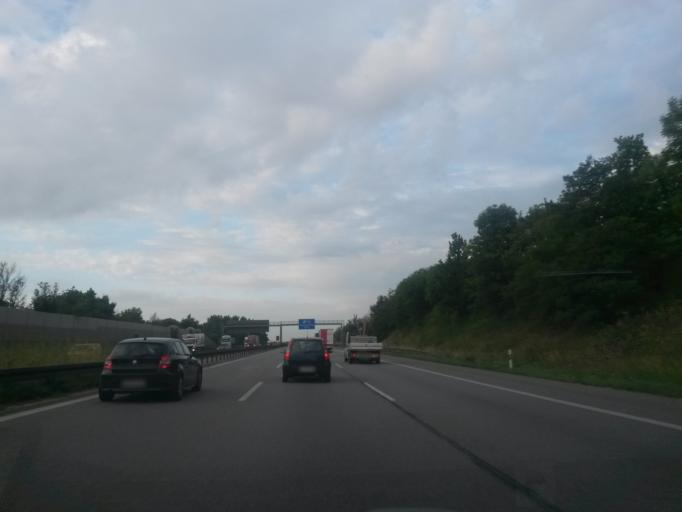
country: DE
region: Bavaria
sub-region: Upper Bavaria
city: Lenting
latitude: 48.7665
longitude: 11.4599
